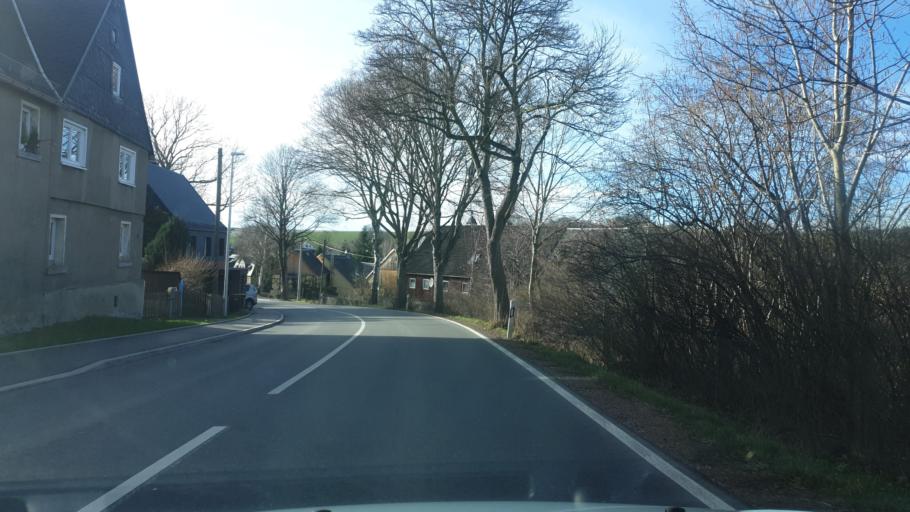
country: DE
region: Saxony
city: Hartenstein
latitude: 50.6682
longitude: 12.6556
